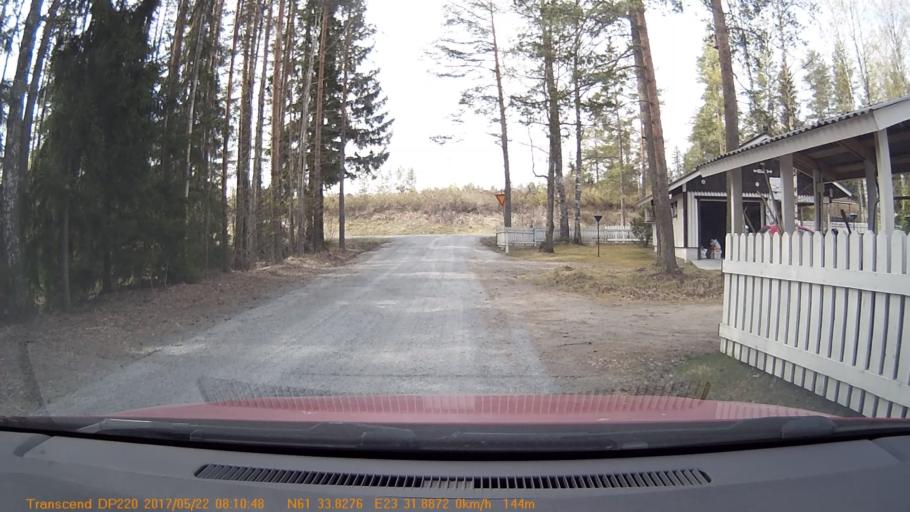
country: FI
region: Pirkanmaa
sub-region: Tampere
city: Yloejaervi
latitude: 61.5638
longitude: 23.5315
